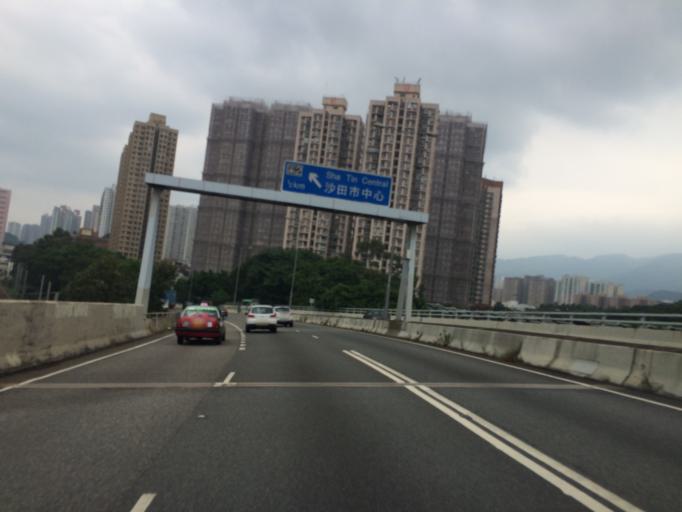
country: HK
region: Sha Tin
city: Sha Tin
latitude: 22.3786
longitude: 114.1846
